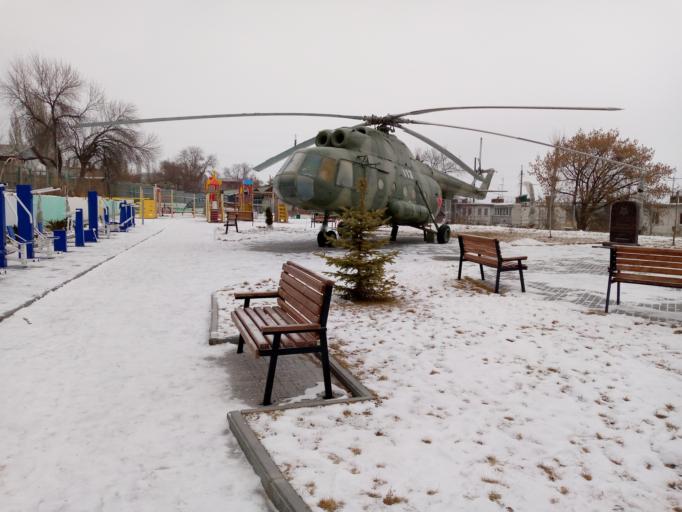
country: RU
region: Saratov
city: Sokolovyy
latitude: 51.3609
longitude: 45.8329
